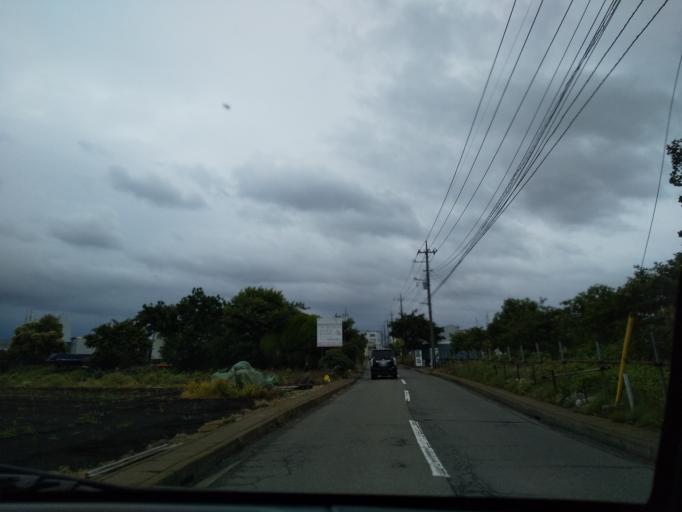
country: JP
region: Kanagawa
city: Minami-rinkan
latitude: 35.4371
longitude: 139.4428
